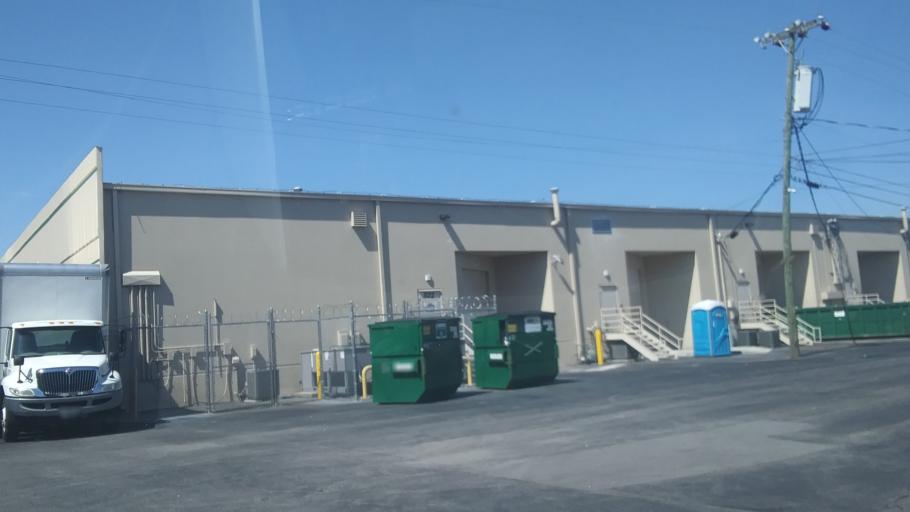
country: US
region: Tennessee
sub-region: Davidson County
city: Oak Hill
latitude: 36.0953
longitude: -86.6834
